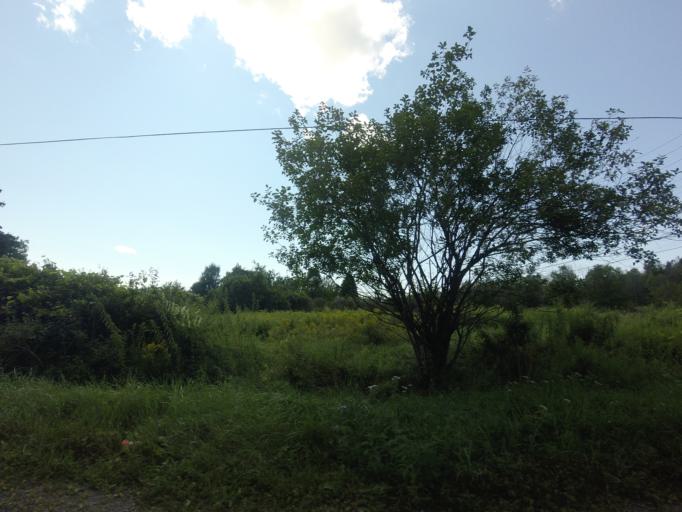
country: CA
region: Ontario
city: Bells Corners
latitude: 45.3419
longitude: -75.8869
